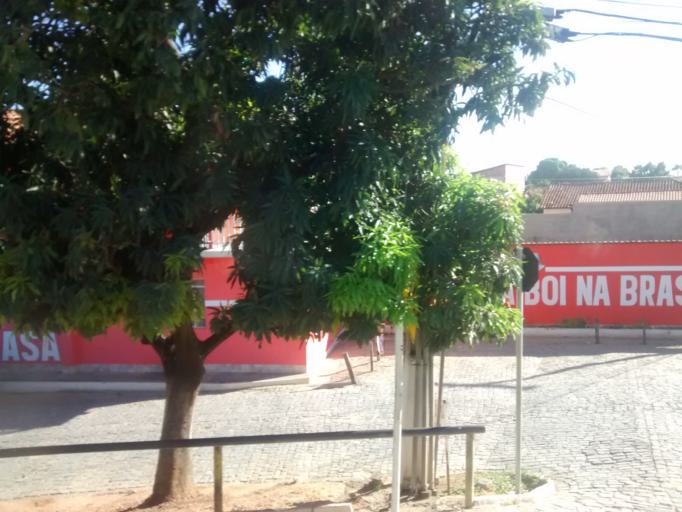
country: BR
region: Bahia
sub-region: Sao Felix Do Coribe
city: Santa Maria da Vitoria
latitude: -13.4017
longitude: -44.1980
